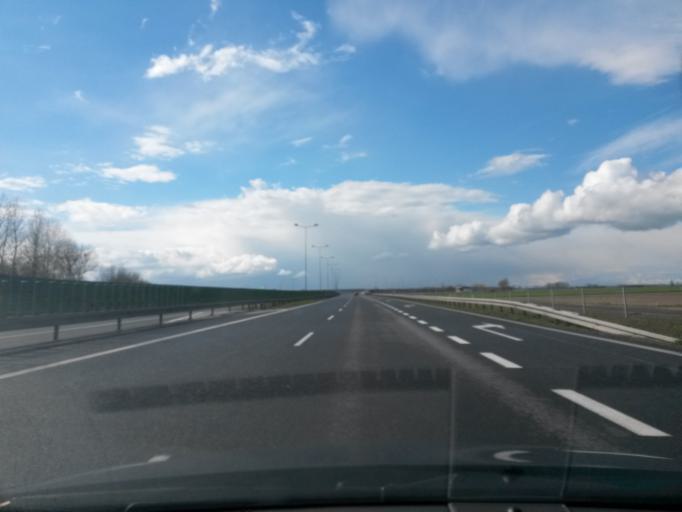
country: PL
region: Greater Poland Voivodeship
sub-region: Powiat wrzesinski
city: Kolaczkowo
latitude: 52.2929
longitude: 17.6594
